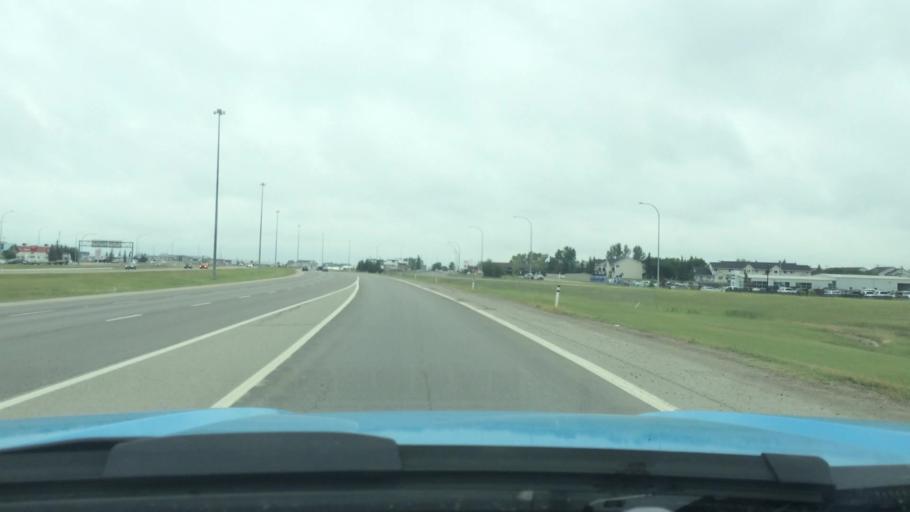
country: CA
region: Alberta
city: Airdrie
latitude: 51.2990
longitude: -114.0022
